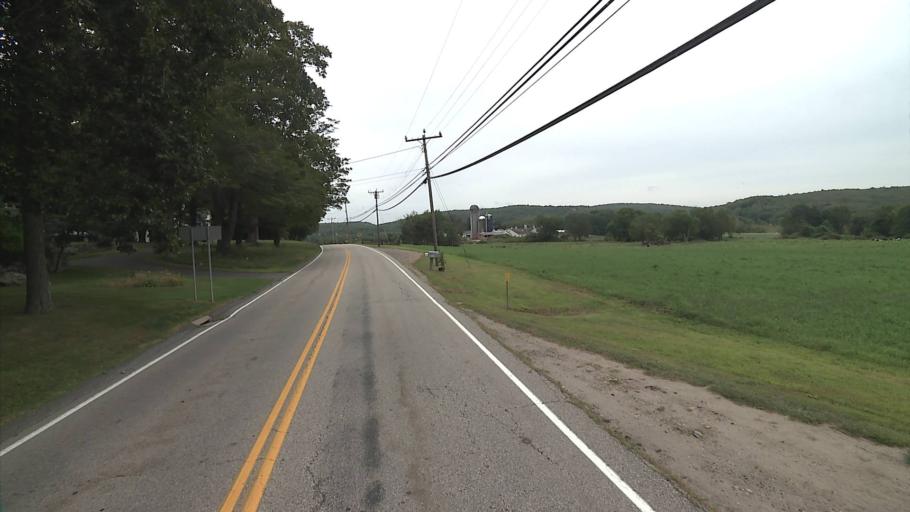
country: US
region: Connecticut
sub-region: Middlesex County
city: Essex Village
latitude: 41.3739
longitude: -72.3473
